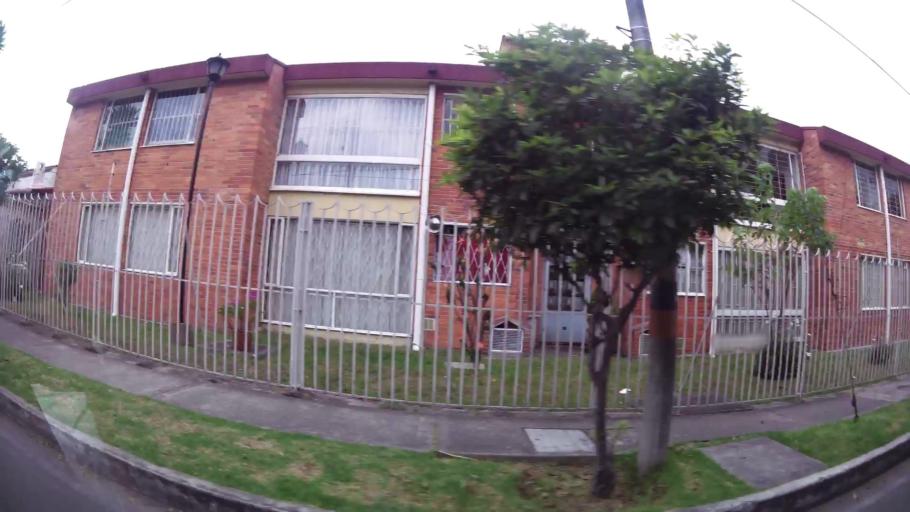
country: CO
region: Bogota D.C.
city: Bogota
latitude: 4.6703
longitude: -74.1229
